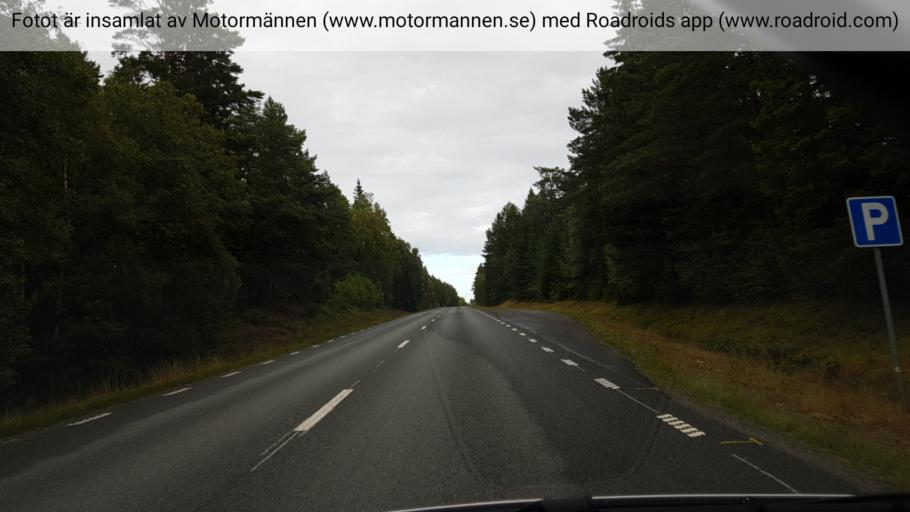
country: SE
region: Vaestra Goetaland
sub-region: Tidaholms Kommun
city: Olofstorp
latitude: 58.2273
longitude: 14.1442
